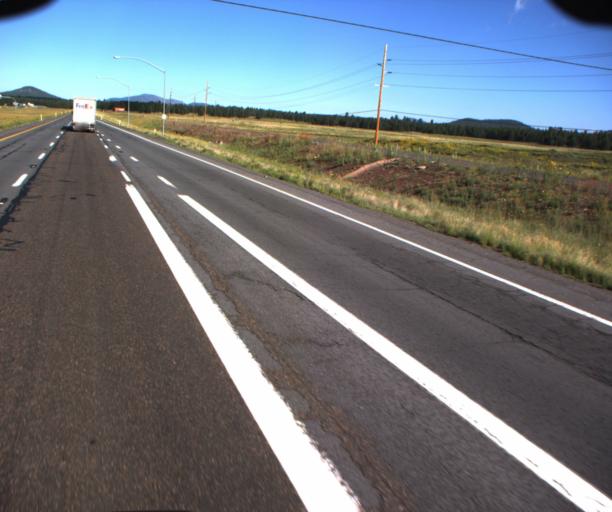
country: US
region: Arizona
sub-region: Coconino County
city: Parks
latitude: 35.2386
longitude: -111.8270
